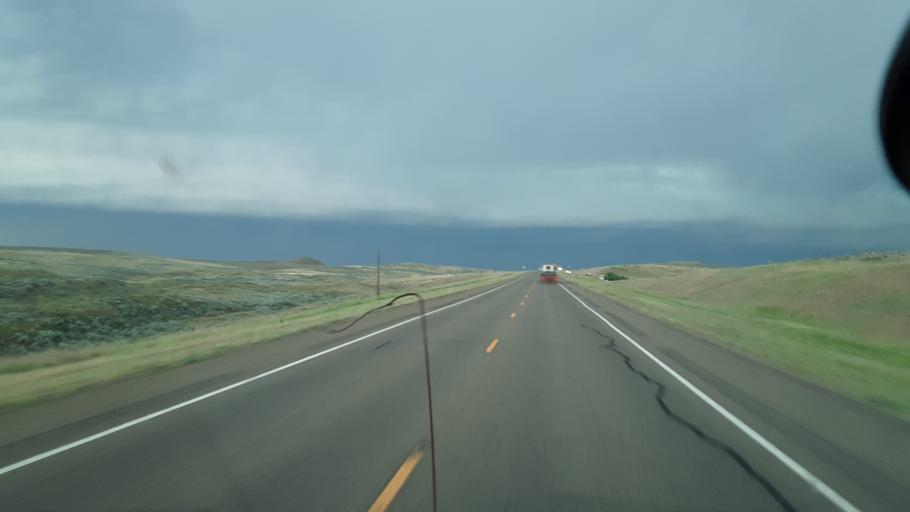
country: US
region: Montana
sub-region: Powder River County
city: Broadus
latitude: 45.3954
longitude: -105.3502
